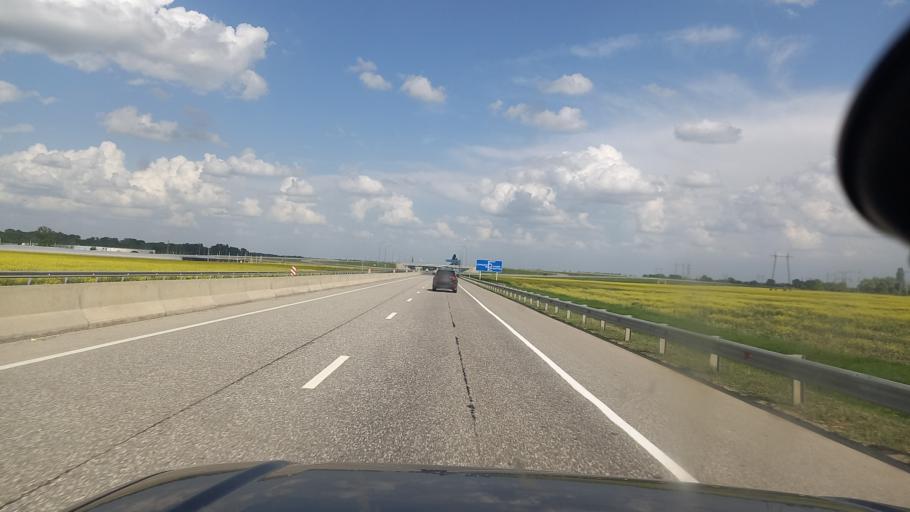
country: RU
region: Chechnya
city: Samashki
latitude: 43.2440
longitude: 45.2803
